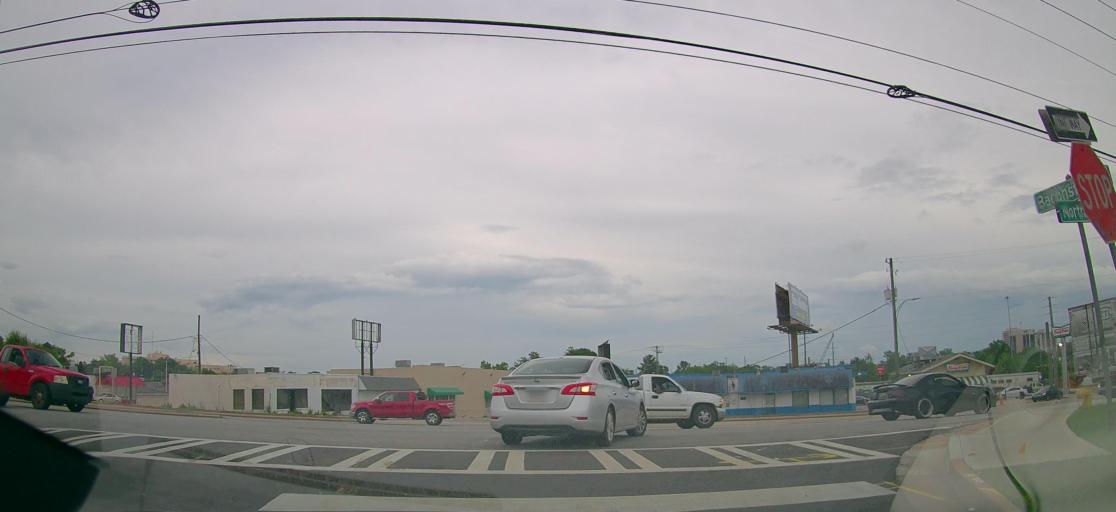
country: US
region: Georgia
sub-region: Bibb County
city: Macon
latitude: 32.8474
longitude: -83.6238
